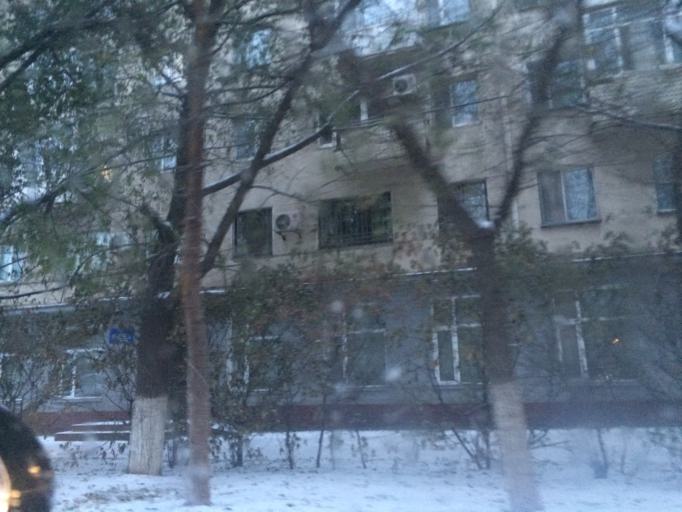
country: KZ
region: Astana Qalasy
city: Astana
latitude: 51.1779
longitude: 71.4103
